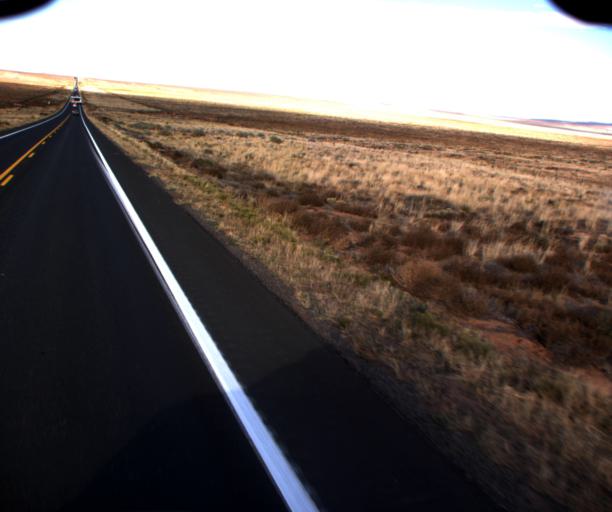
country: US
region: Arizona
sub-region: Apache County
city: Lukachukai
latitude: 36.9617
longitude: -109.4067
